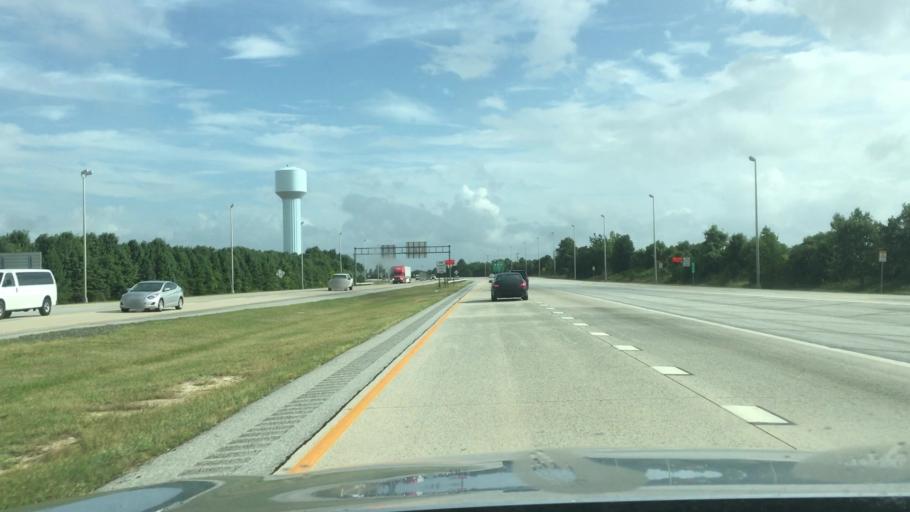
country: US
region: Delaware
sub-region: New Castle County
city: Delaware City
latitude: 39.5228
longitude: -75.6513
